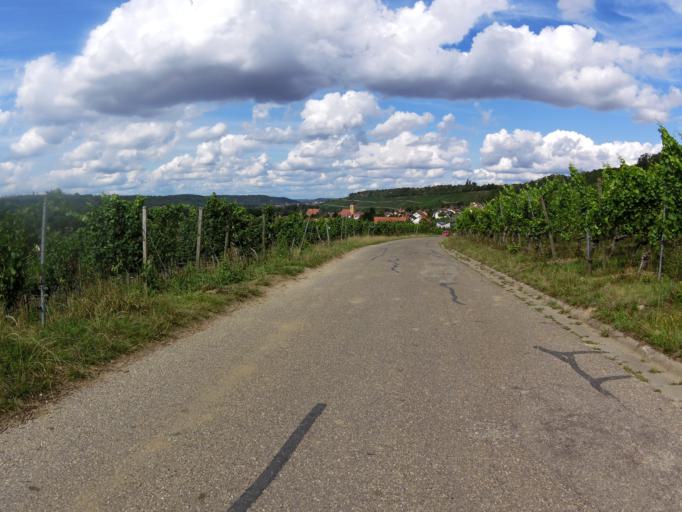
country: DE
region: Bavaria
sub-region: Regierungsbezirk Unterfranken
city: Sommerhausen
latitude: 49.6988
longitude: 10.0311
